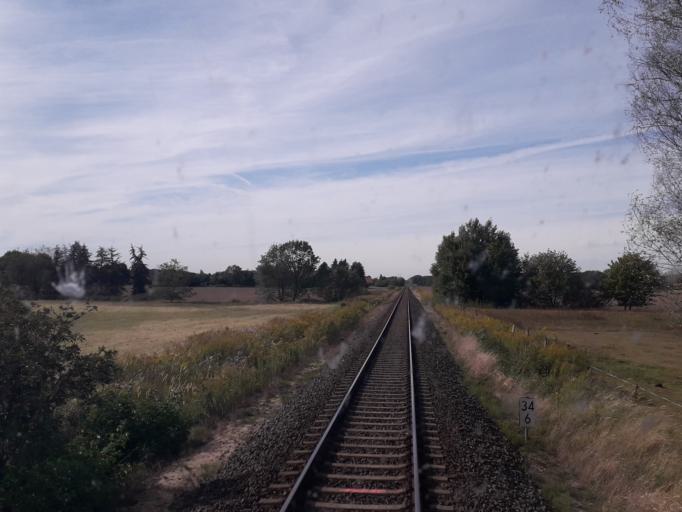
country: DE
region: Brandenburg
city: Kremmen
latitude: 52.7411
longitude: 13.0720
